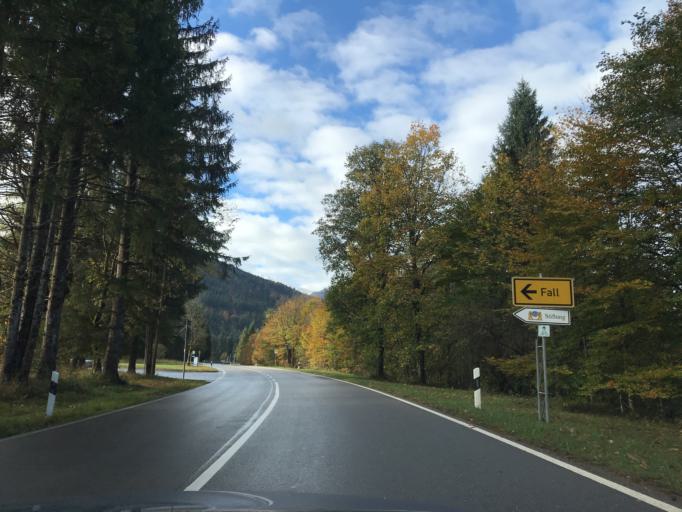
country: DE
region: Bavaria
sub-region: Upper Bavaria
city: Jachenau
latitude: 47.5713
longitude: 11.5311
